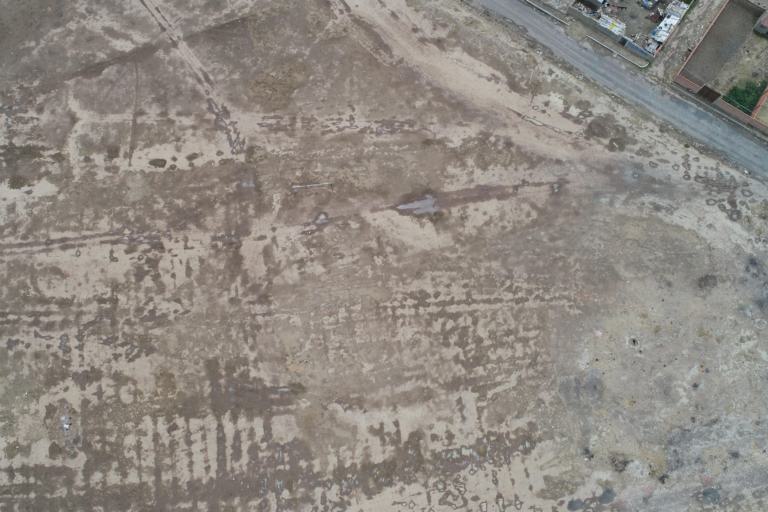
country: BO
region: La Paz
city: Achacachi
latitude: -16.0522
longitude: -68.6879
